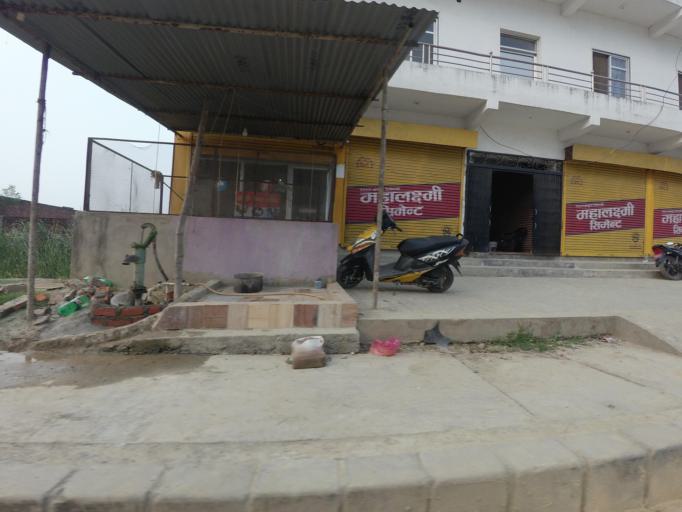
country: NP
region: Western Region
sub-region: Lumbini Zone
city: Bhairahawa
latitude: 27.5186
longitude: 83.4424
